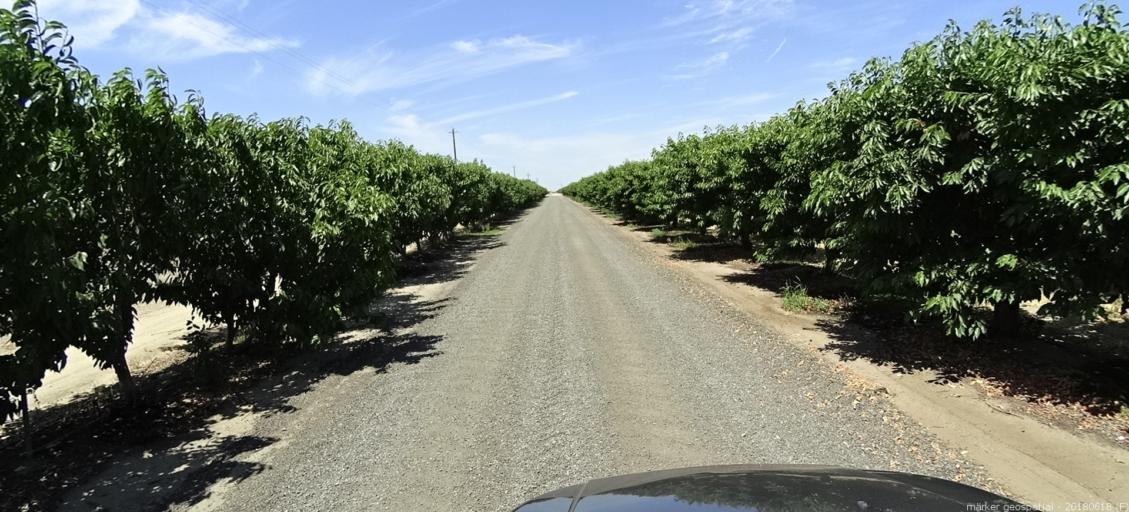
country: US
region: California
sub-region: Madera County
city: Parkwood
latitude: 36.8876
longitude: -120.1437
